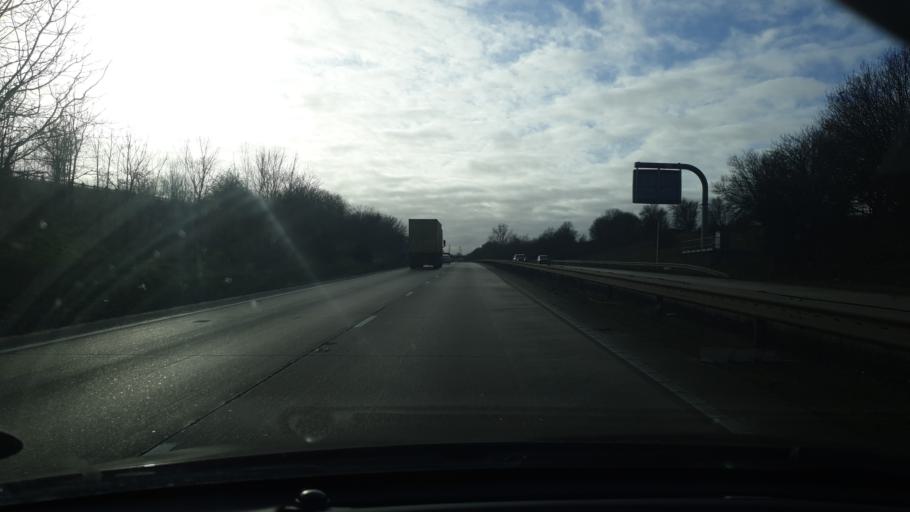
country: GB
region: England
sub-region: Suffolk
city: Bramford
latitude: 52.0550
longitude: 1.1020
